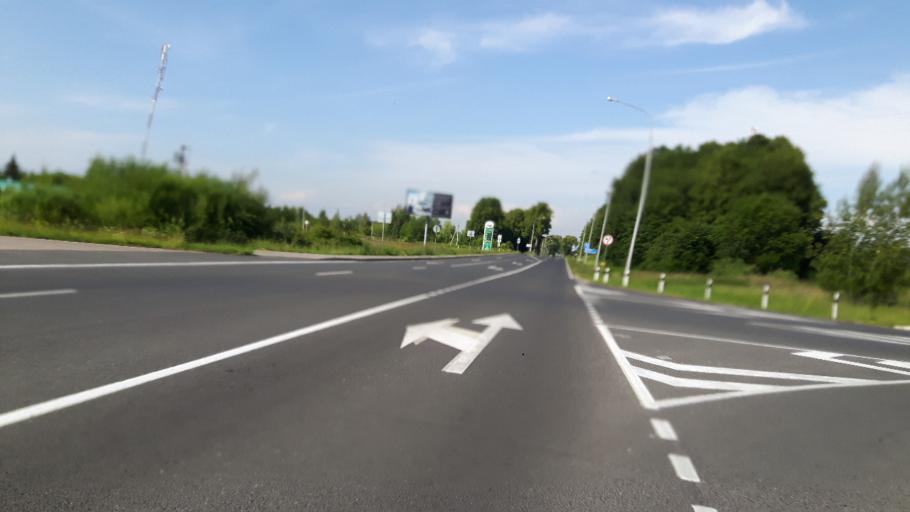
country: RU
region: Kaliningrad
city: Mamonovo
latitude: 54.4505
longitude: 19.9176
